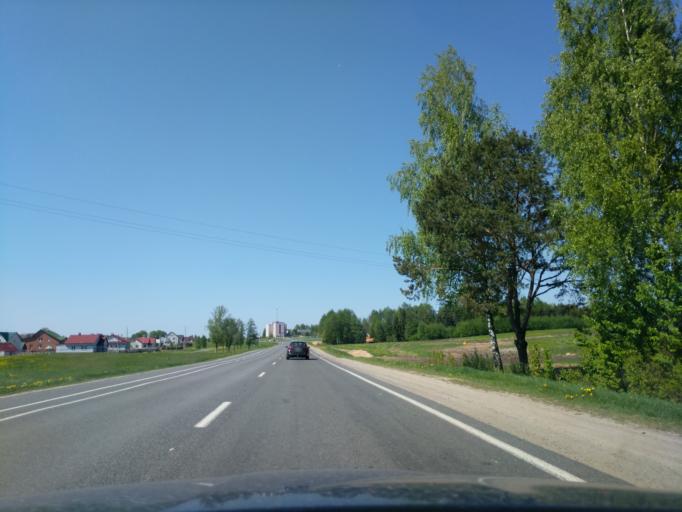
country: BY
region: Minsk
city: Myadzyel
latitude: 54.8860
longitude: 26.9302
